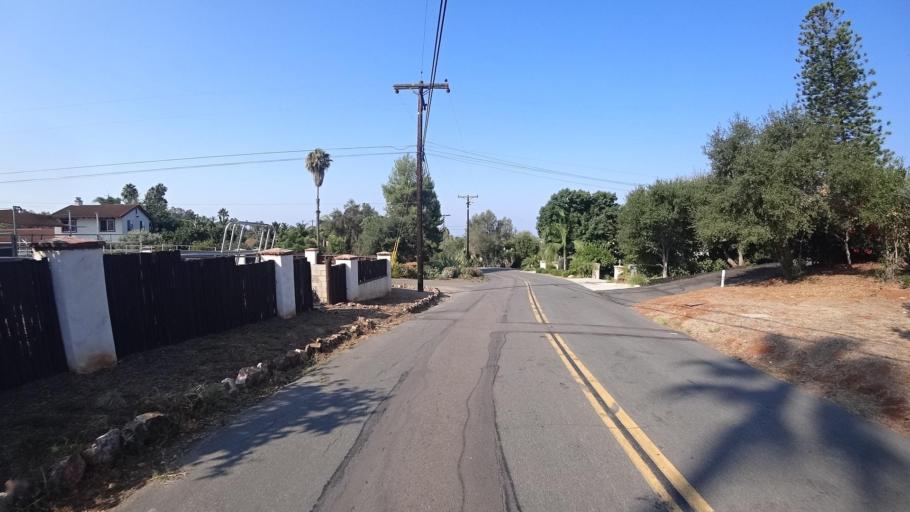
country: US
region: California
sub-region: San Diego County
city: Vista
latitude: 33.2331
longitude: -117.2179
